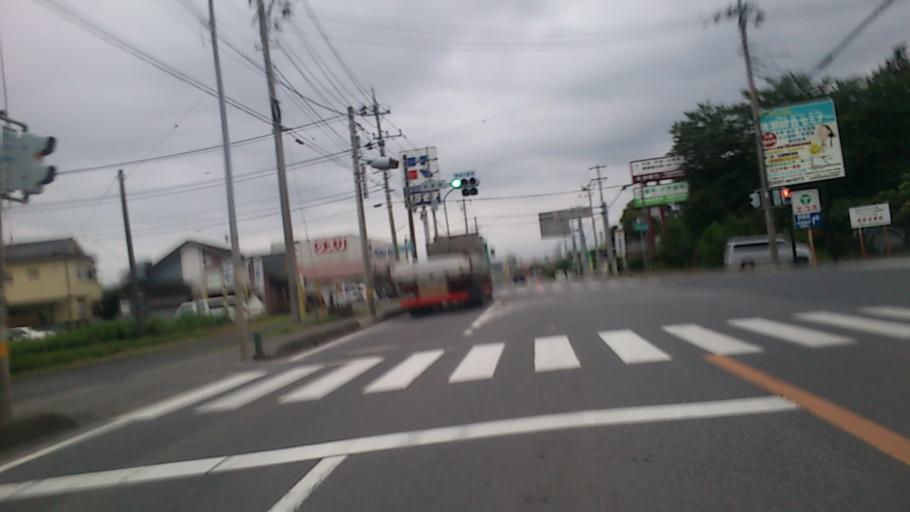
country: JP
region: Ibaraki
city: Iwai
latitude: 36.1001
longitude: 139.8988
